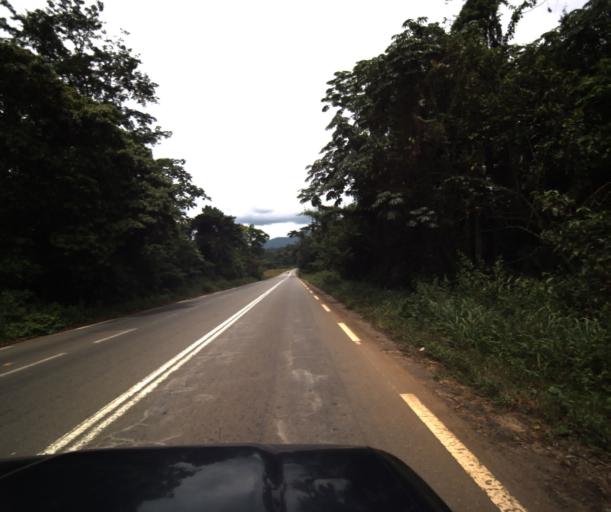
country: CM
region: Centre
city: Eseka
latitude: 3.8753
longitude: 10.8196
